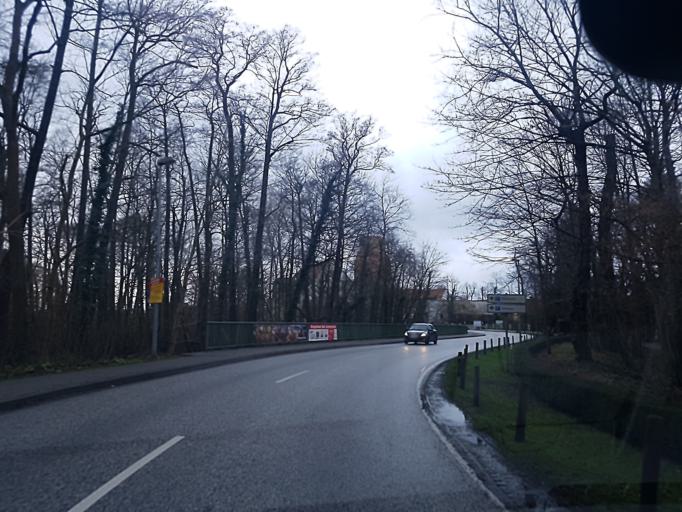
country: DE
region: Brandenburg
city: Bad Liebenwerda
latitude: 51.5152
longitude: 13.4011
